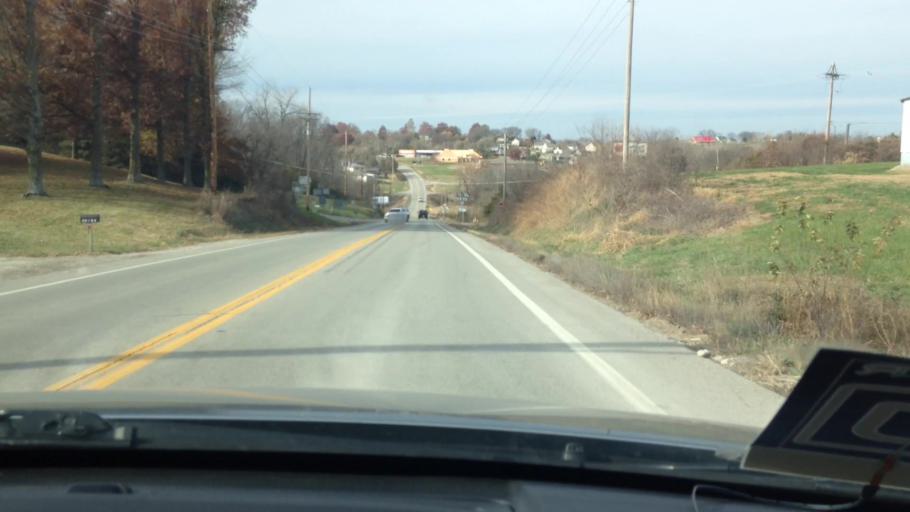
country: US
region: Missouri
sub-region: Platte County
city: Weston
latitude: 39.4168
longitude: -94.8902
